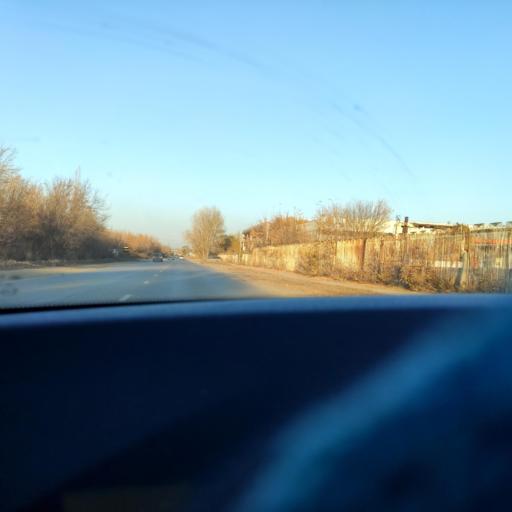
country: RU
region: Samara
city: Petra-Dubrava
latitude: 53.2562
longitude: 50.2817
